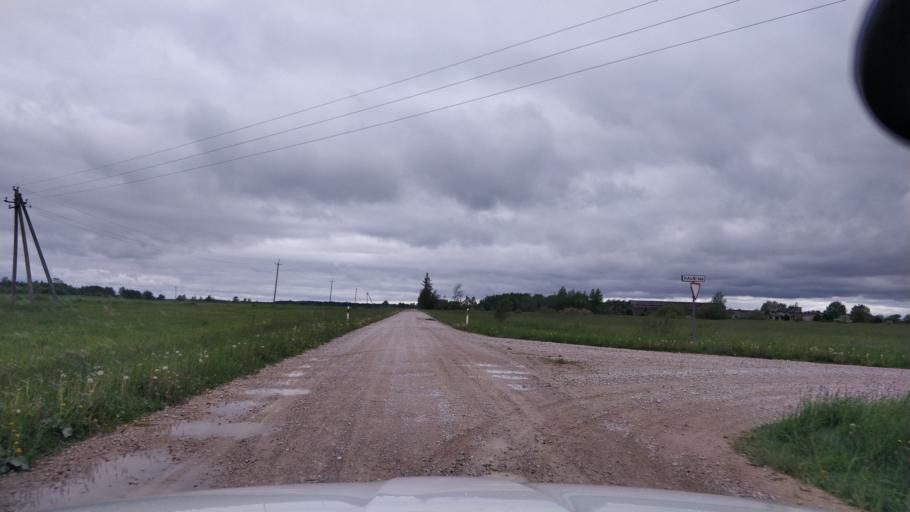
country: EE
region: Raplamaa
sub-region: Maerjamaa vald
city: Marjamaa
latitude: 58.7149
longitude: 24.2418
